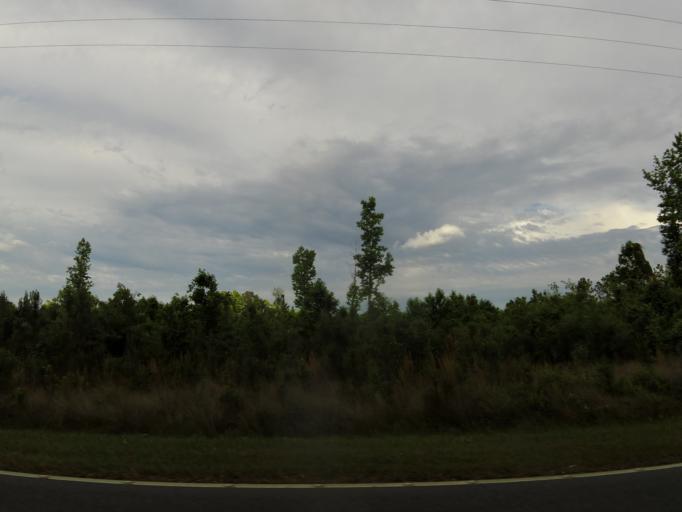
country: US
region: South Carolina
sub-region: Jasper County
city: Ridgeland
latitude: 32.4533
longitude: -81.1061
